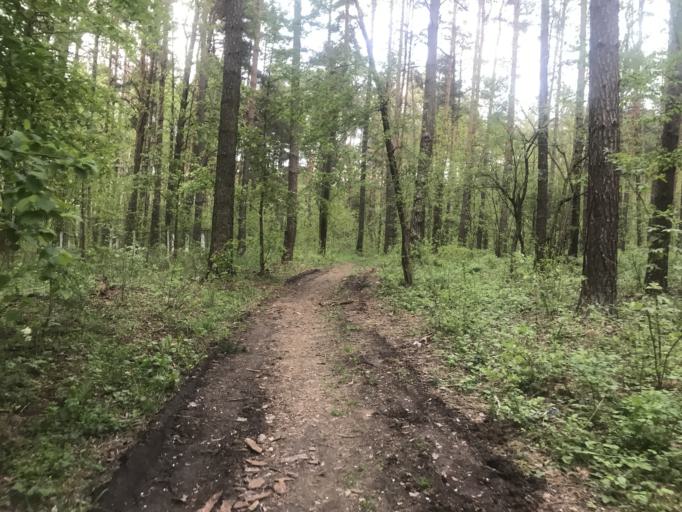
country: BY
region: Minsk
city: Zhdanovichy
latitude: 53.9535
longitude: 27.4235
